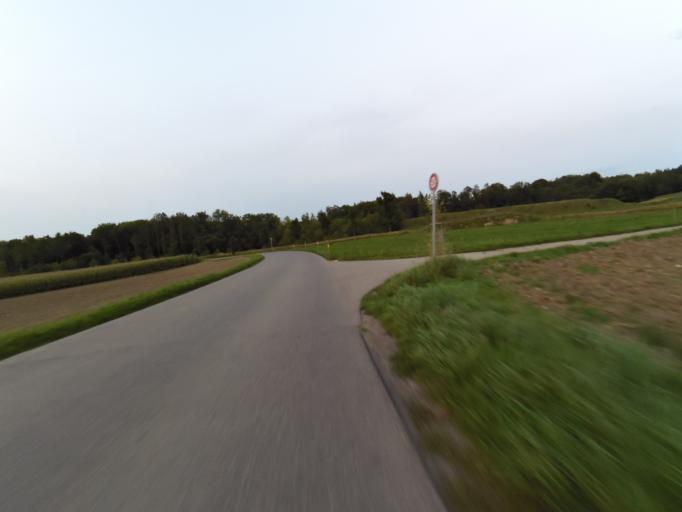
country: CH
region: Thurgau
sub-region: Frauenfeld District
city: Gachnang
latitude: 47.5476
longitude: 8.8755
